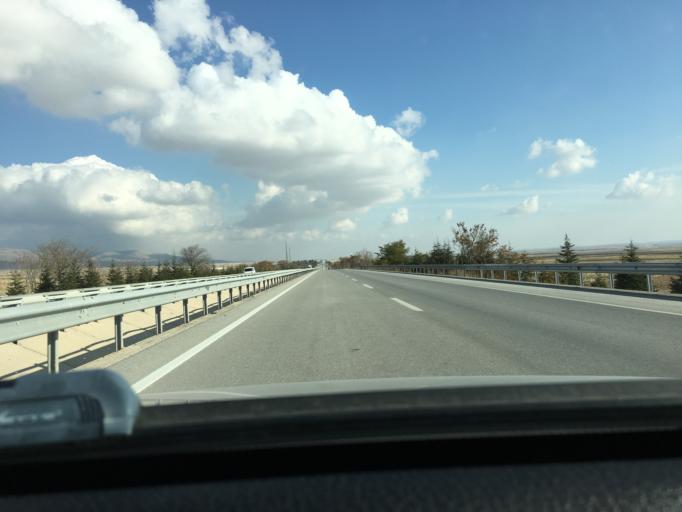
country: TR
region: Eskisehir
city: Kaymaz
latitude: 39.4809
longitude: 31.3014
